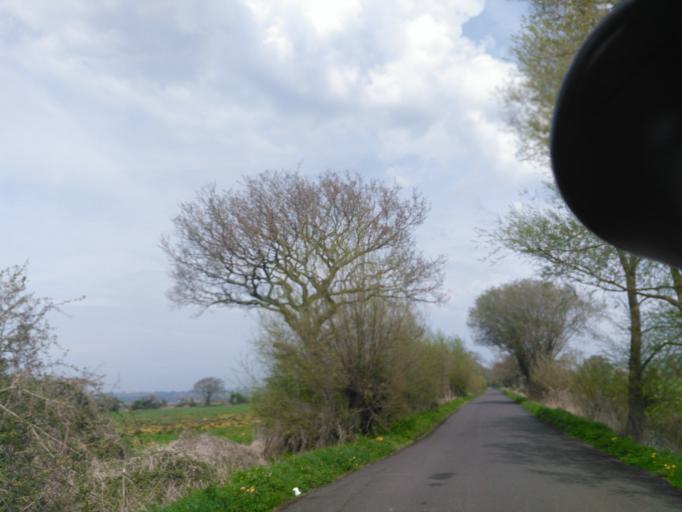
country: GB
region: England
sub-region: Somerset
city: Langport
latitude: 51.1000
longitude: -2.8194
